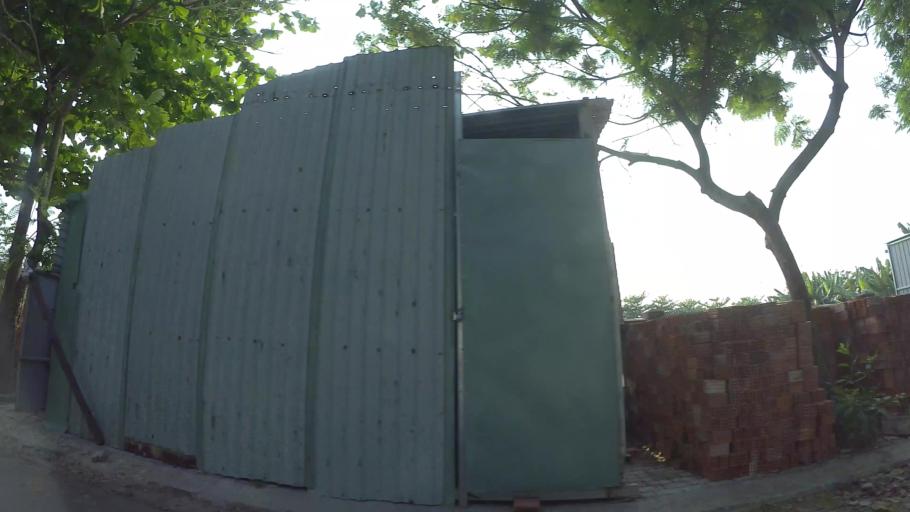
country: VN
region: Da Nang
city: Cam Le
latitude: 16.0227
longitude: 108.2046
